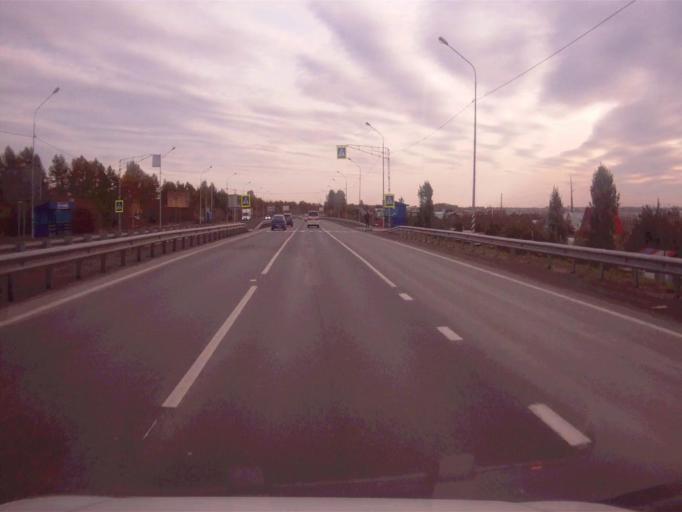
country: RU
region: Chelyabinsk
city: Novosineglazovskiy
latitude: 55.0317
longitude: 61.4454
